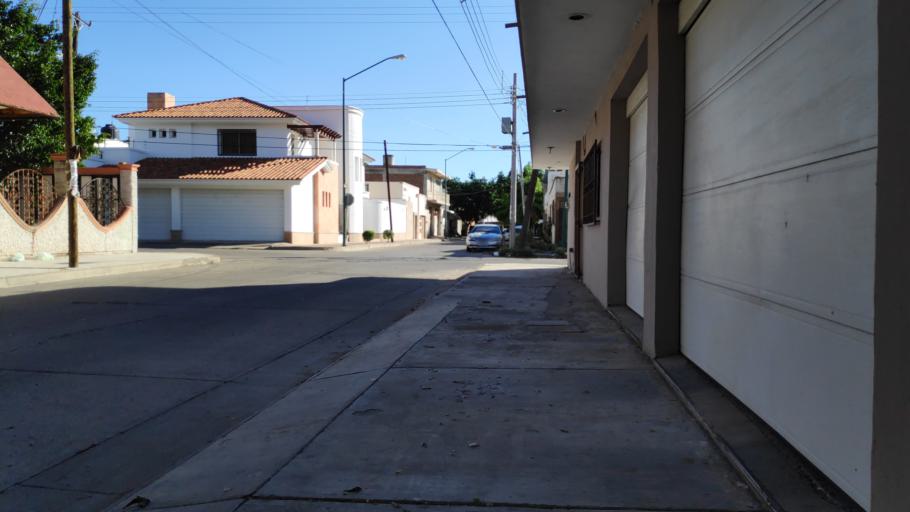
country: MX
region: Sinaloa
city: Culiacan
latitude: 24.7954
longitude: -107.3993
